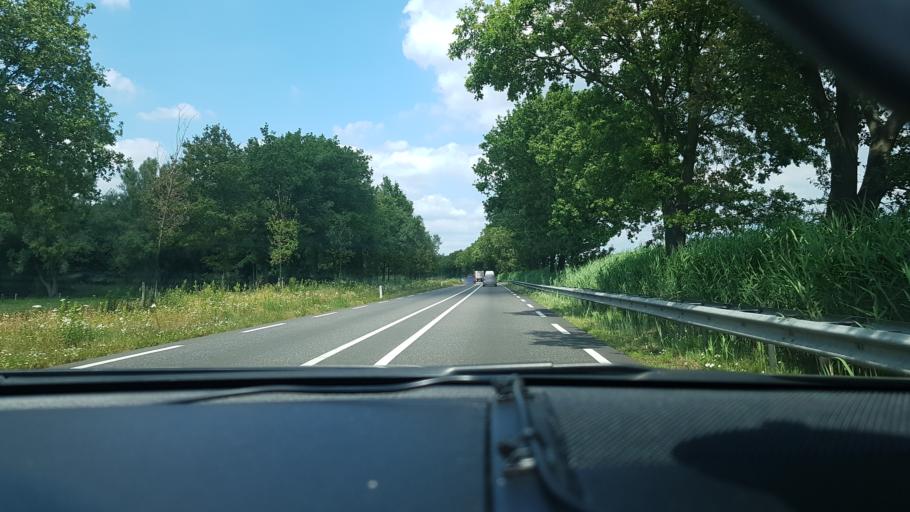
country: NL
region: North Brabant
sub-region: Gemeente Helmond
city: Helmond
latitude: 51.4372
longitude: 5.6936
